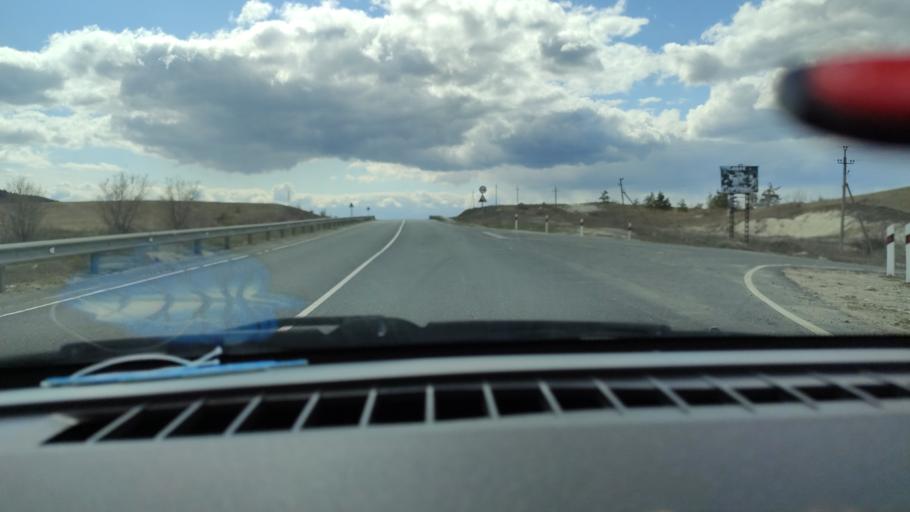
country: RU
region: Saratov
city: Alekseyevka
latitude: 52.3196
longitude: 47.9220
